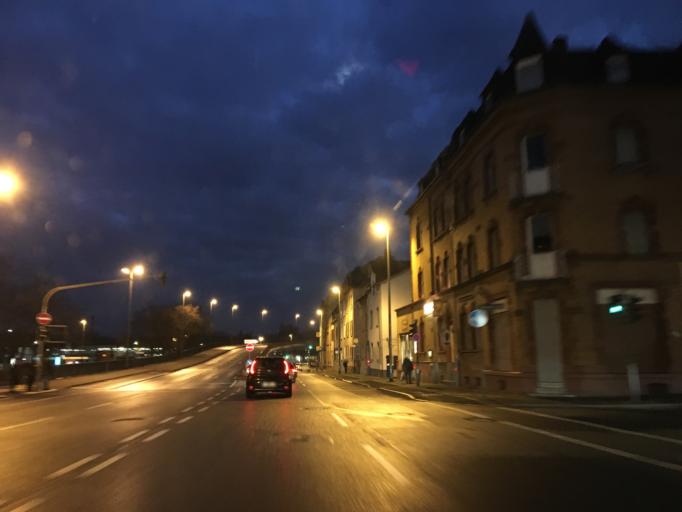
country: DE
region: Hesse
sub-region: Regierungsbezirk Darmstadt
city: Frankfurt am Main
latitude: 50.1615
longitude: 8.6481
